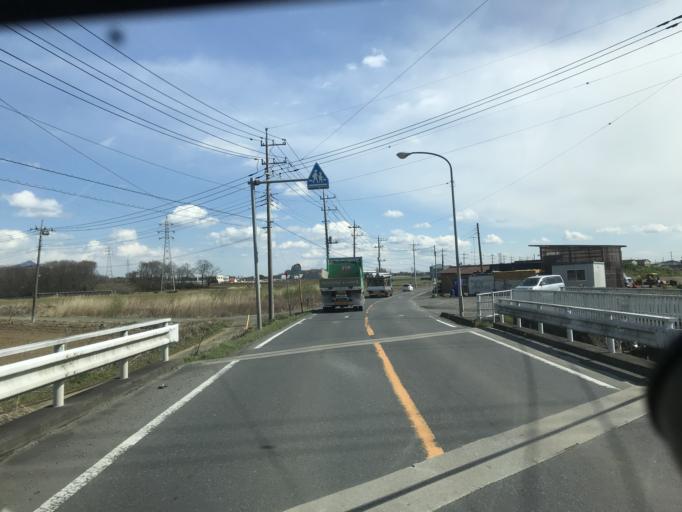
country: JP
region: Ibaraki
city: Yuki
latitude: 36.2439
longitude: 139.9279
